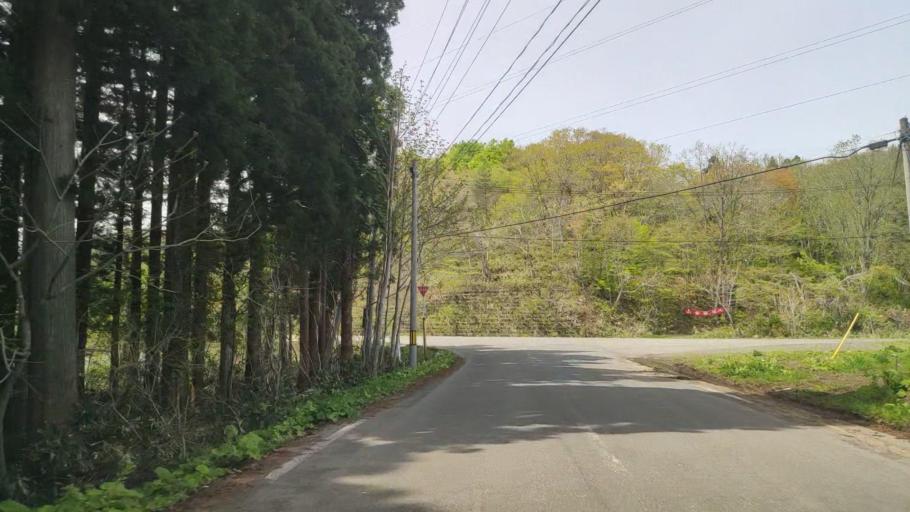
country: JP
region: Aomori
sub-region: Misawa Shi
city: Inuotose
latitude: 40.7904
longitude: 141.0996
